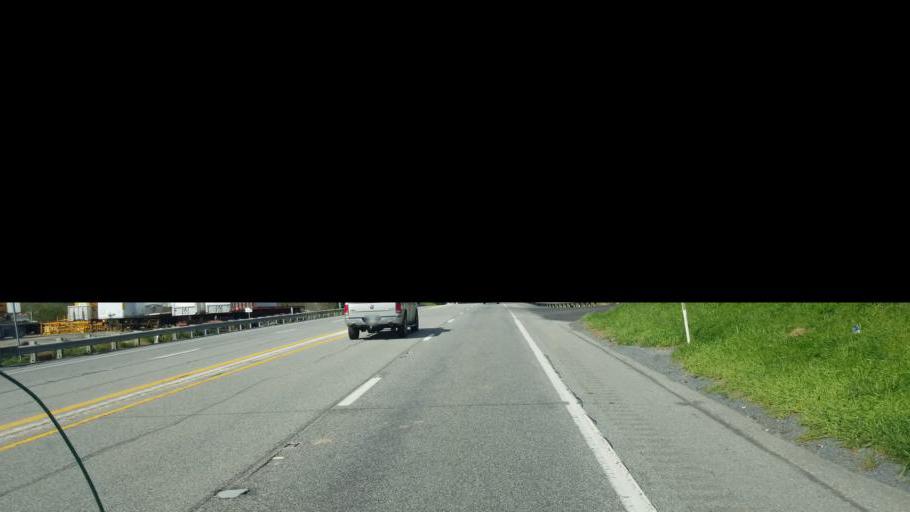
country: US
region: Pennsylvania
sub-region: Bedford County
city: Earlston
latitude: 40.0171
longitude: -78.3257
